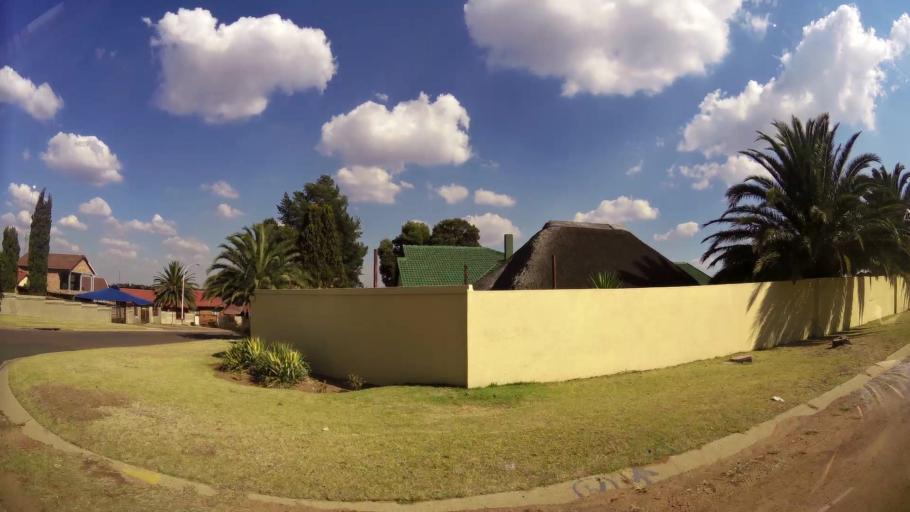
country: ZA
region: Mpumalanga
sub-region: Nkangala District Municipality
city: Witbank
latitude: -25.9306
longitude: 29.2470
